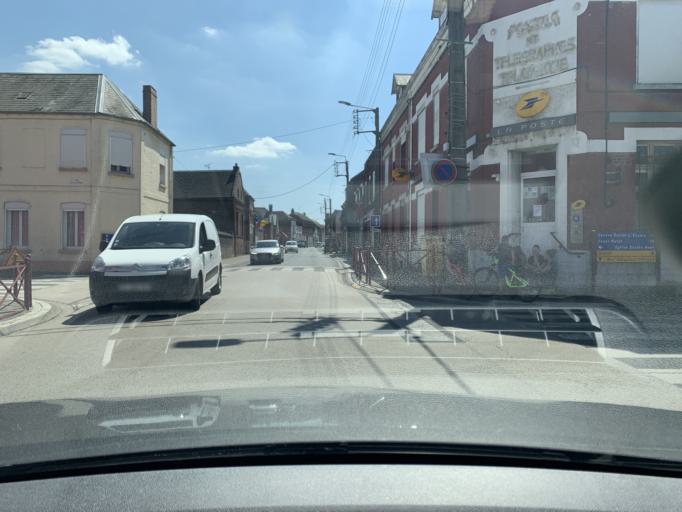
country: FR
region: Nord-Pas-de-Calais
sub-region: Departement du Nord
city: Beauvois-en-Cambresis
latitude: 50.1378
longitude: 3.3802
